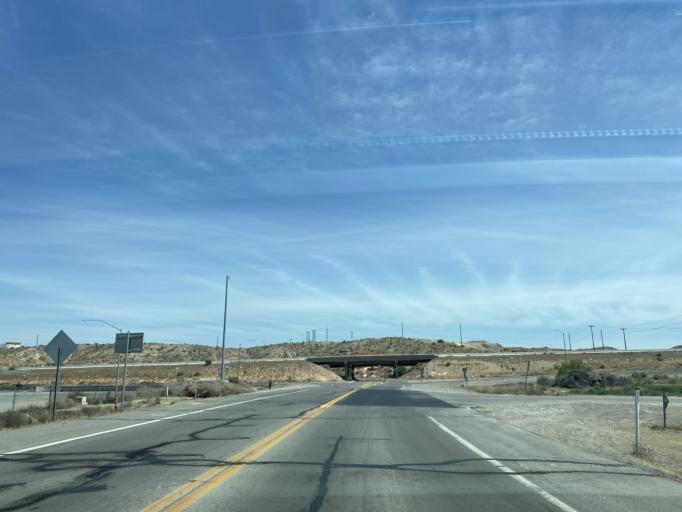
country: US
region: Nevada
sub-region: Clark County
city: Moapa Town
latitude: 36.6617
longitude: -114.5757
